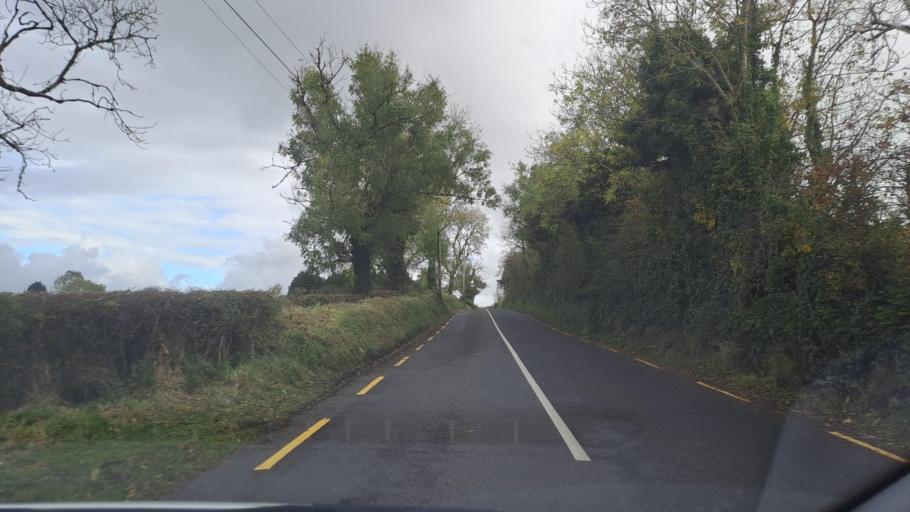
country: IE
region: Ulster
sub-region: An Cabhan
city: Mullagh
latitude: 53.8170
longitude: -6.9885
